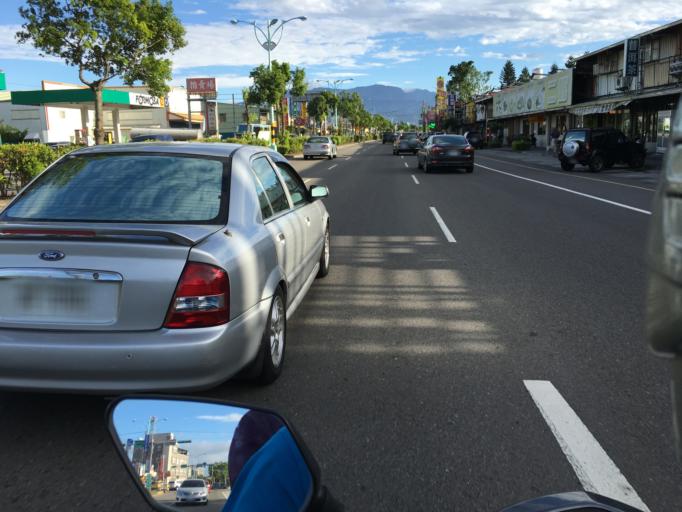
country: TW
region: Taiwan
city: Daxi
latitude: 24.8690
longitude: 121.2209
